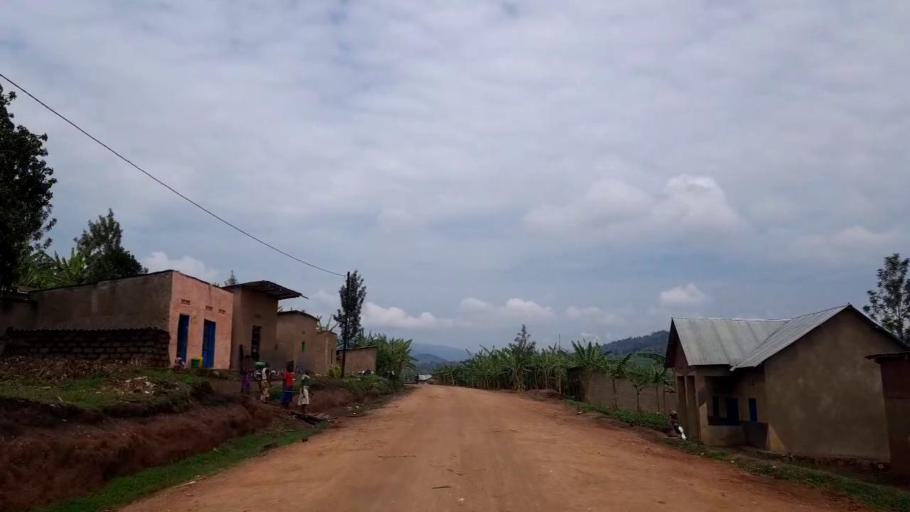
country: RW
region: Northern Province
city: Byumba
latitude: -1.4983
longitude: 30.2270
